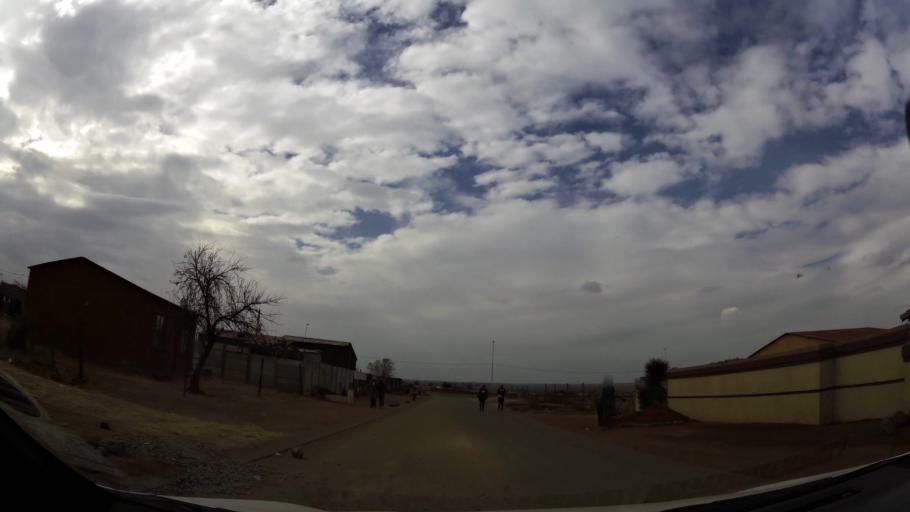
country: ZA
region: Gauteng
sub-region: Ekurhuleni Metropolitan Municipality
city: Germiston
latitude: -26.3960
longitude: 28.1558
